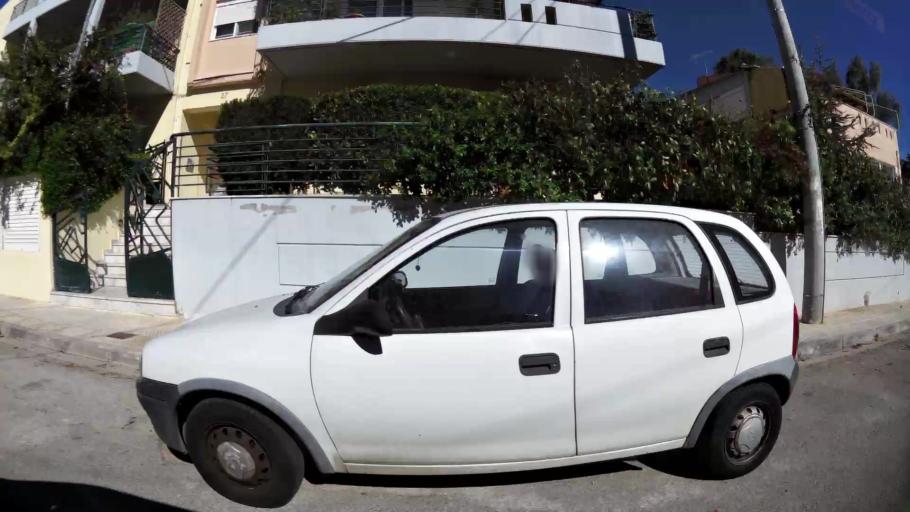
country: GR
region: Attica
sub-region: Nomarchia Anatolikis Attikis
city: Gerakas
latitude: 38.0058
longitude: 23.8577
